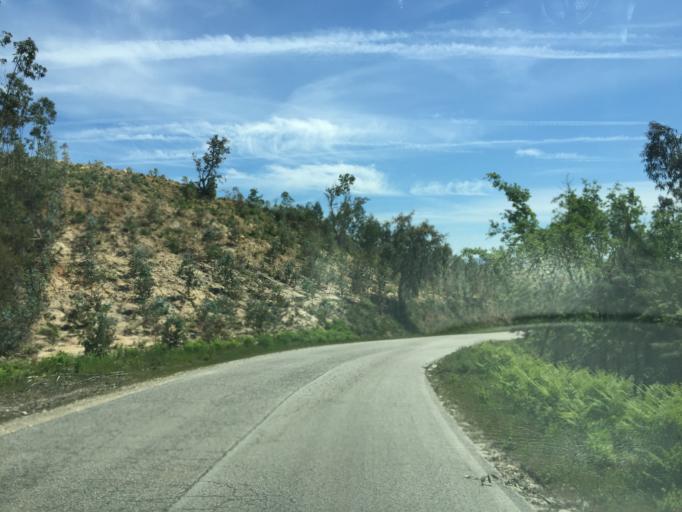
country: PT
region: Coimbra
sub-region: Soure
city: Soure
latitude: 40.0545
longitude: -8.6764
